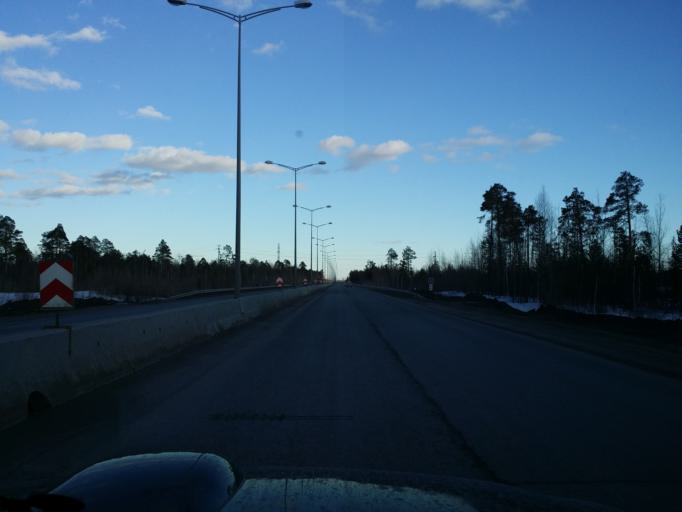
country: RU
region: Khanty-Mansiyskiy Avtonomnyy Okrug
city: Nizhnevartovsk
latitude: 61.0028
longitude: 76.4154
